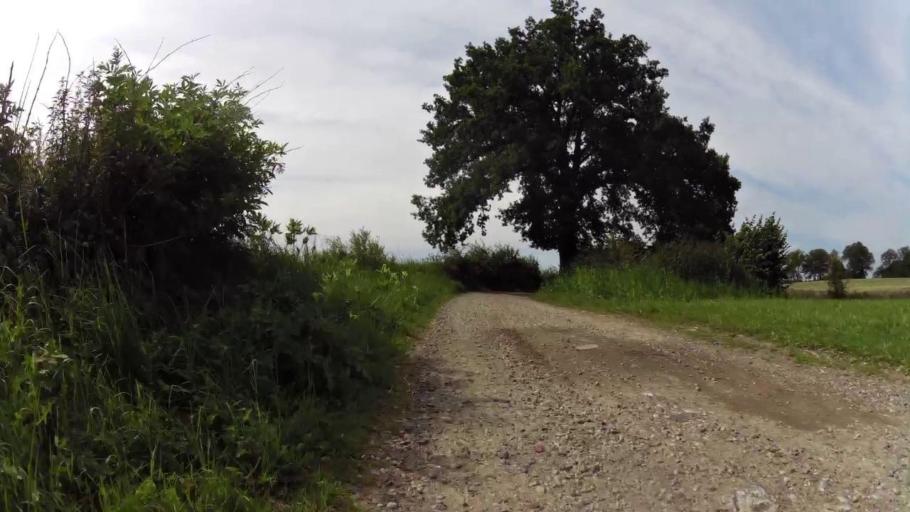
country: PL
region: West Pomeranian Voivodeship
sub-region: Powiat lobeski
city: Wegorzyno
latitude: 53.5393
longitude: 15.6035
